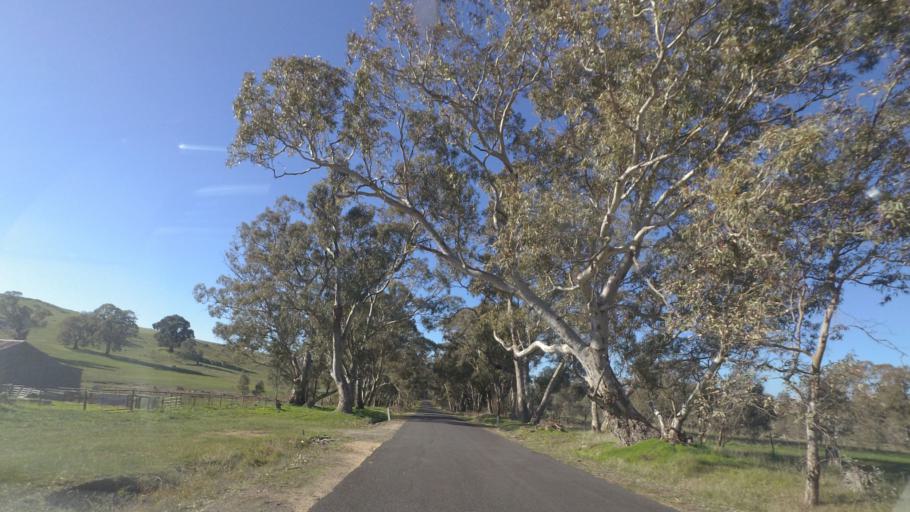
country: AU
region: Victoria
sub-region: Mount Alexander
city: Castlemaine
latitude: -36.9687
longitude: 144.3180
